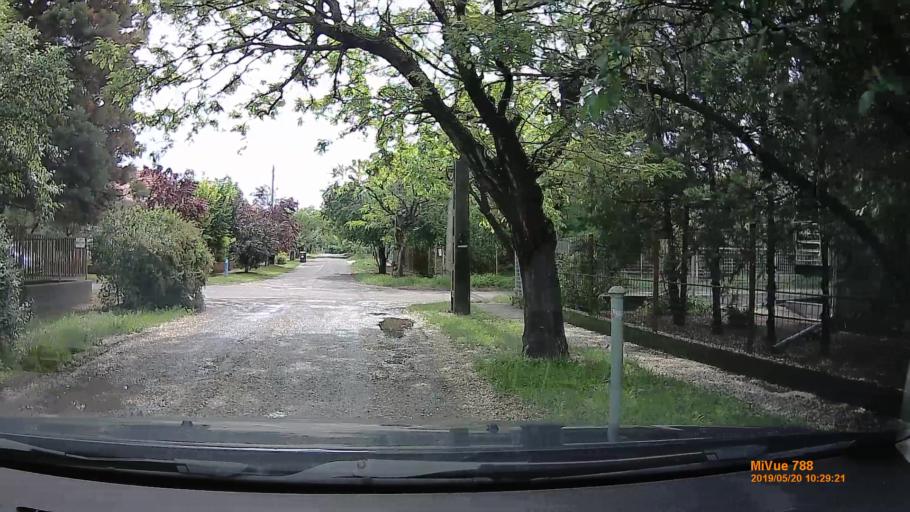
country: HU
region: Budapest
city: Budapest XVII. keruelet
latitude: 47.4575
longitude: 19.2389
